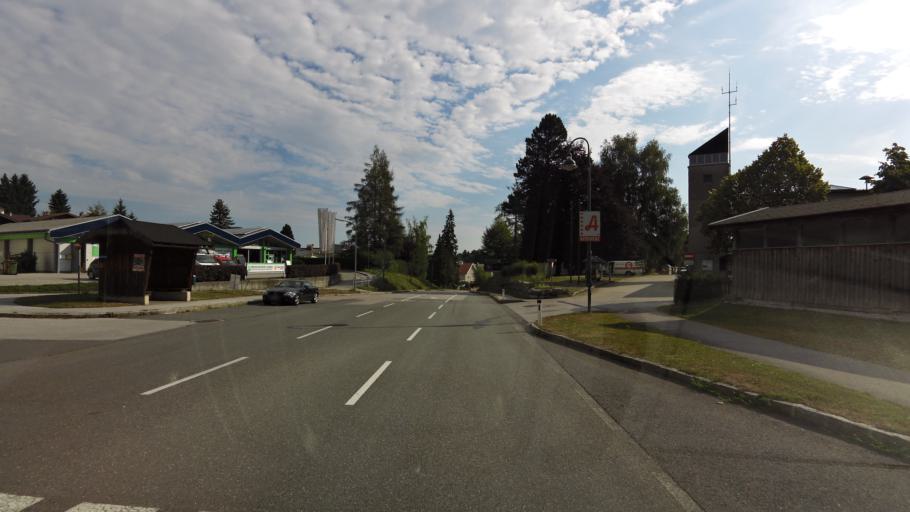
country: AT
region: Salzburg
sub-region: Politischer Bezirk Salzburg-Umgebung
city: Henndorf am Wallersee
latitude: 47.8952
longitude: 13.1826
